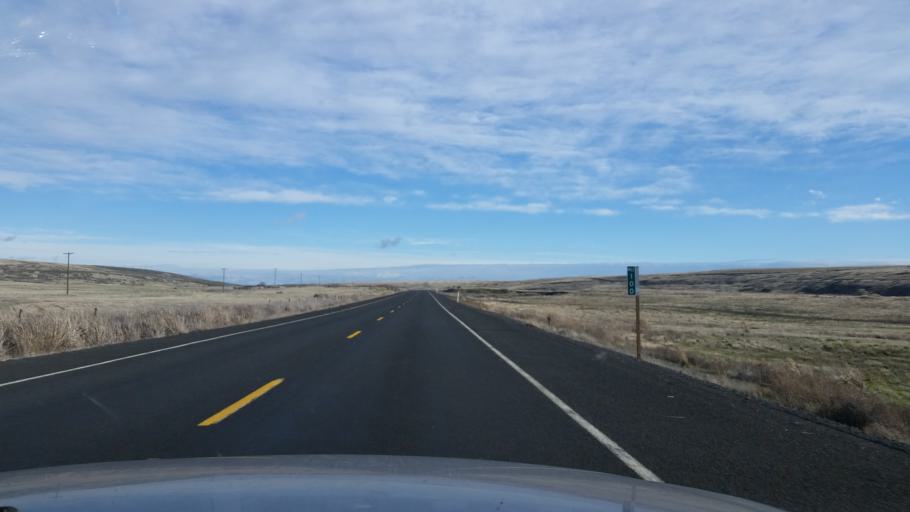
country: US
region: Washington
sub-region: Adams County
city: Ritzville
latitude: 47.3477
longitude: -118.5672
